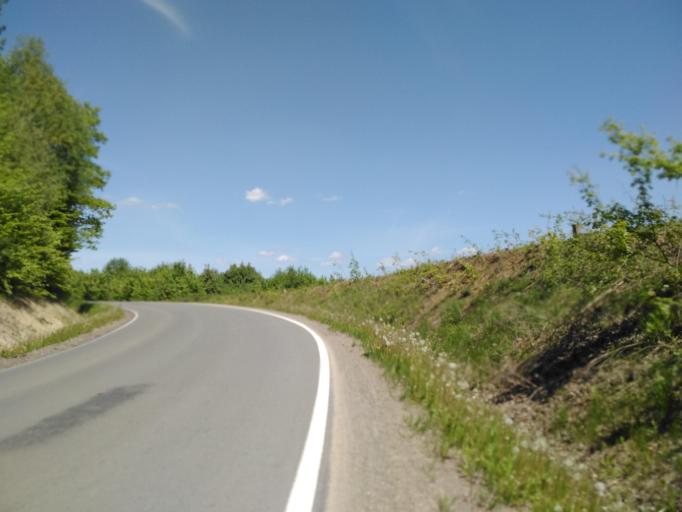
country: PL
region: Subcarpathian Voivodeship
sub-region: Powiat krosnienski
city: Chorkowka
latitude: 49.6161
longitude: 21.7190
